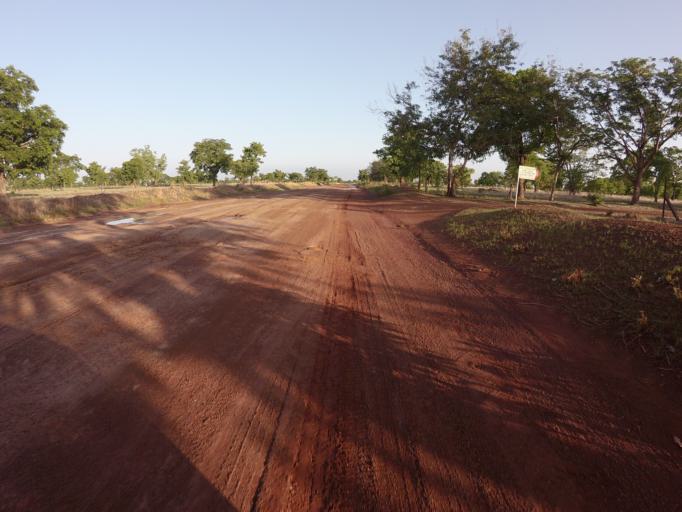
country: TG
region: Savanes
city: Sansanne-Mango
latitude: 10.2985
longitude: -0.0894
